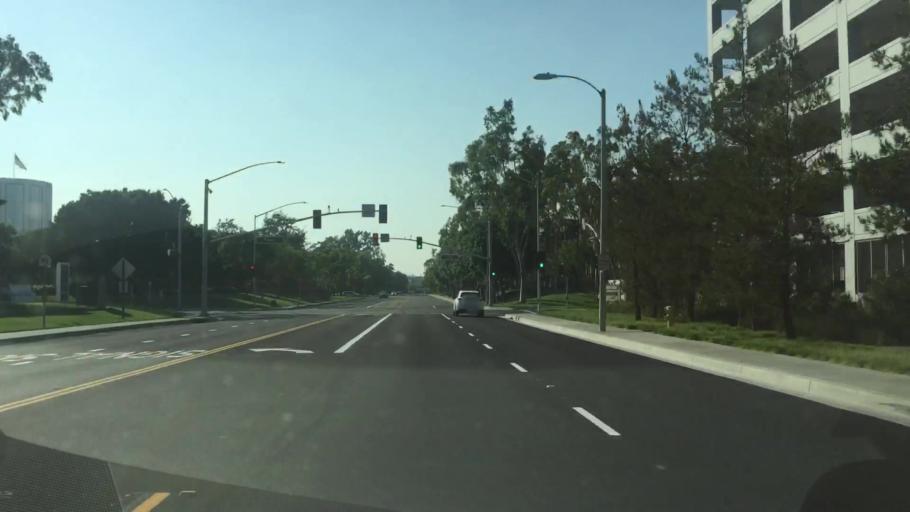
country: US
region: California
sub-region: Orange County
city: Irvine
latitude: 33.6698
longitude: -117.8524
